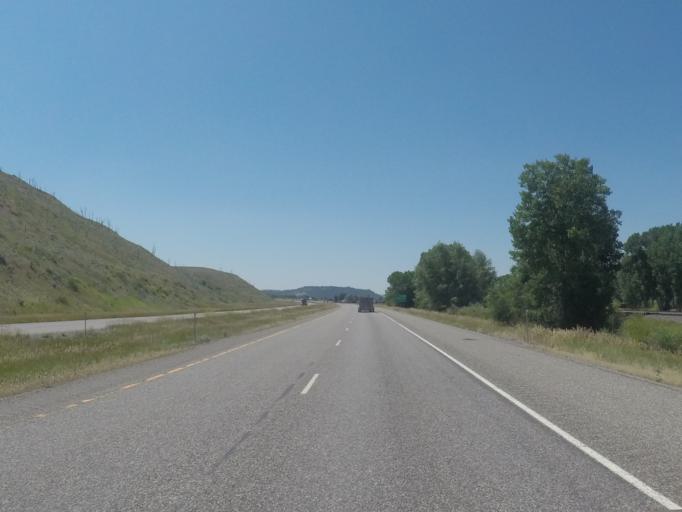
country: US
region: Montana
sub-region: Stillwater County
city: Absarokee
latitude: 45.7083
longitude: -109.5152
